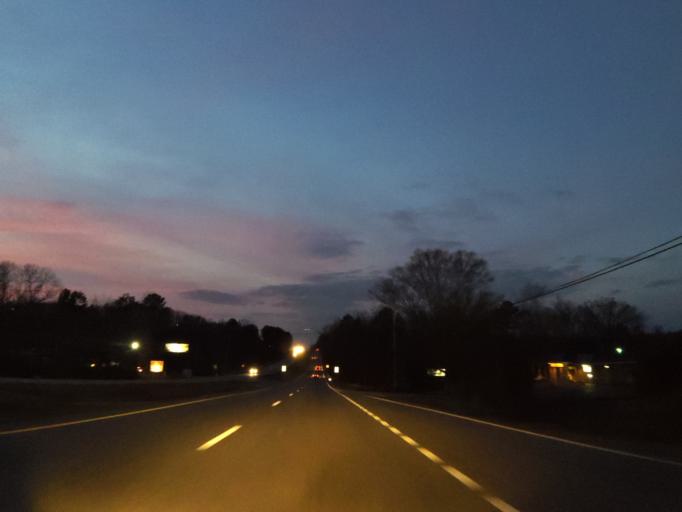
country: US
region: Tennessee
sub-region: Polk County
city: Benton
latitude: 35.1279
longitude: -84.7207
